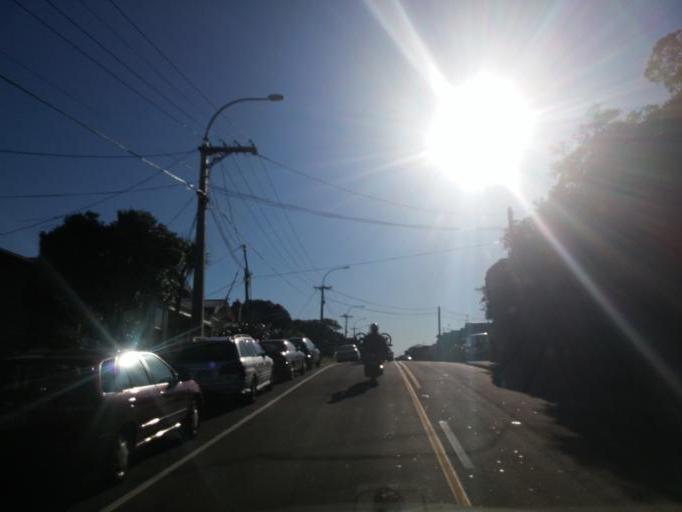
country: NZ
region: Wellington
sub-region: Wellington City
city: Brooklyn
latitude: -41.3186
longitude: 174.7753
